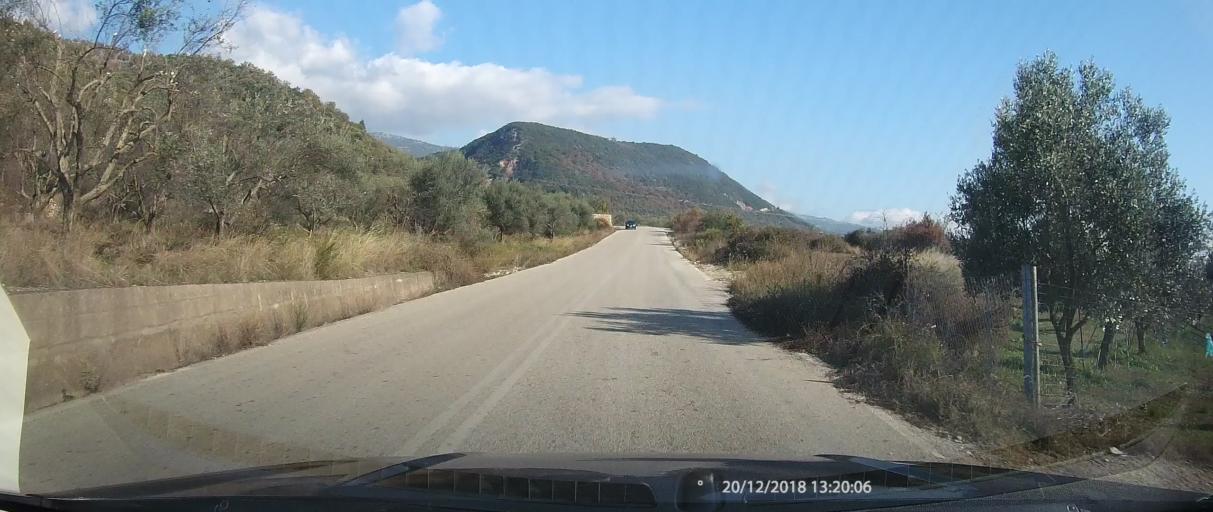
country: GR
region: West Greece
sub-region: Nomos Aitolias kai Akarnanias
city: Paravola
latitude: 38.6155
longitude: 21.5436
